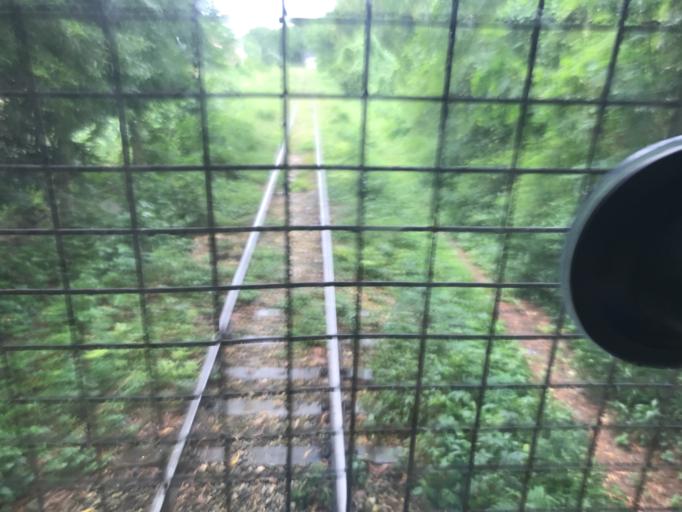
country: MM
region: Bago
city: Paungde
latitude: 18.6861
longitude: 95.4002
